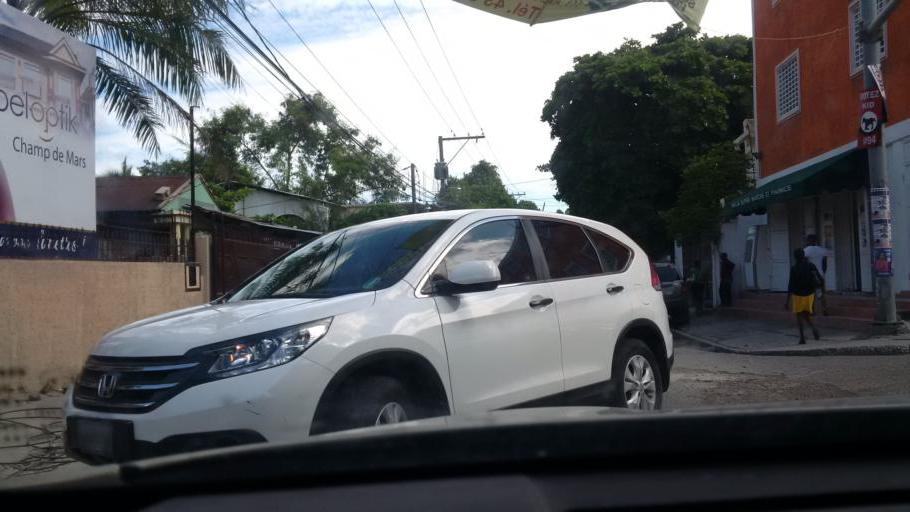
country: HT
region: Ouest
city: Port-au-Prince
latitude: 18.5375
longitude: -72.3232
